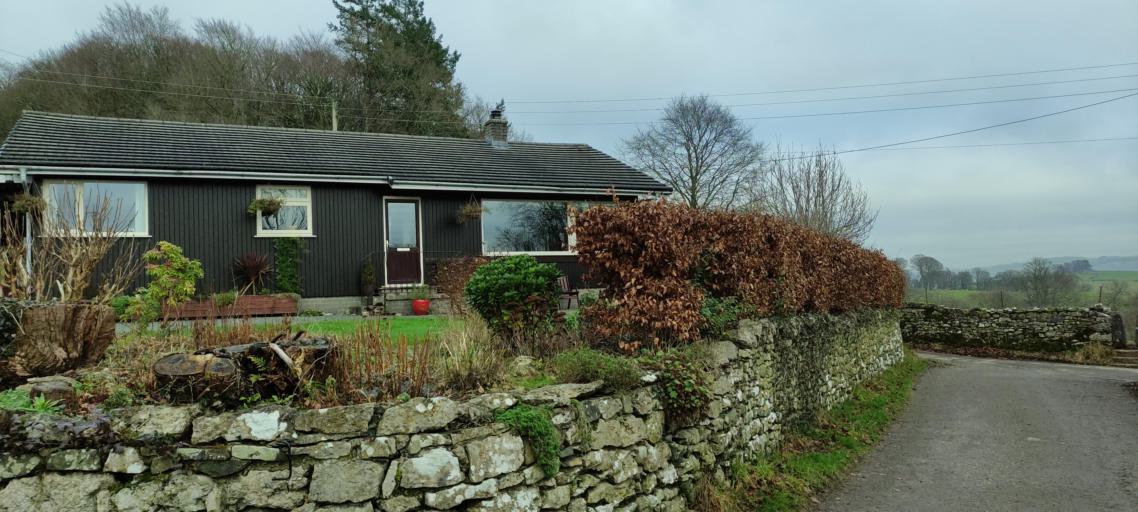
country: GB
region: England
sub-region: Cumbria
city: Milnthorpe
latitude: 54.2173
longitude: -2.7860
